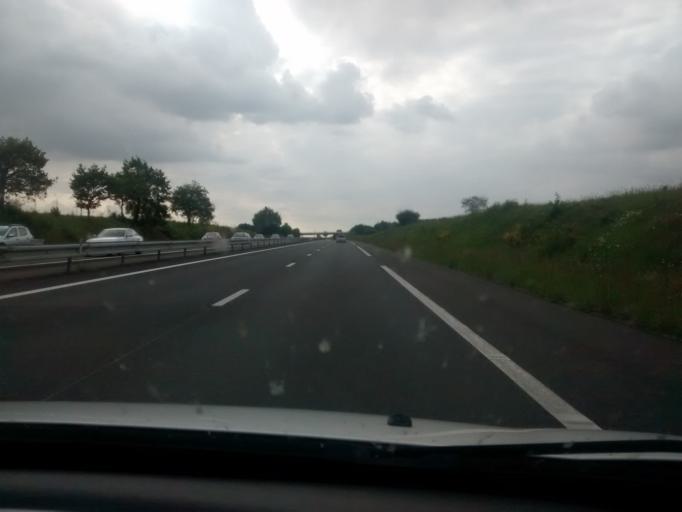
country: FR
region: Pays de la Loire
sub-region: Departement de la Mayenne
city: Sainte-Suzanne
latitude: 48.0306
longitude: -0.3503
